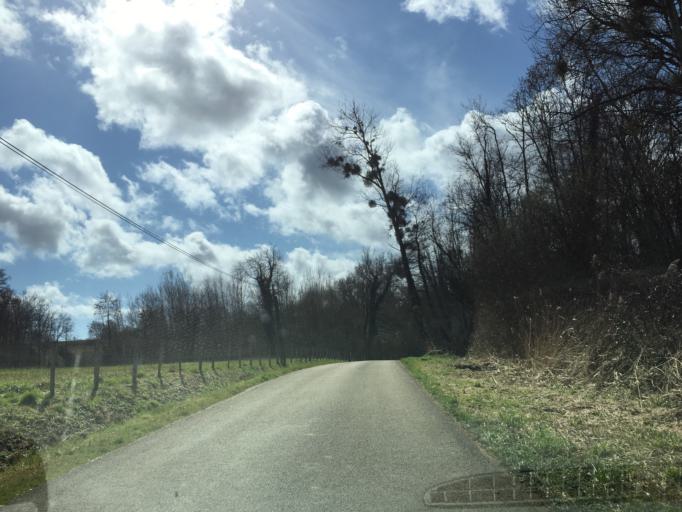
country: FR
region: Bourgogne
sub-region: Departement de l'Yonne
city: Charbuy
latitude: 47.8193
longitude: 3.4257
